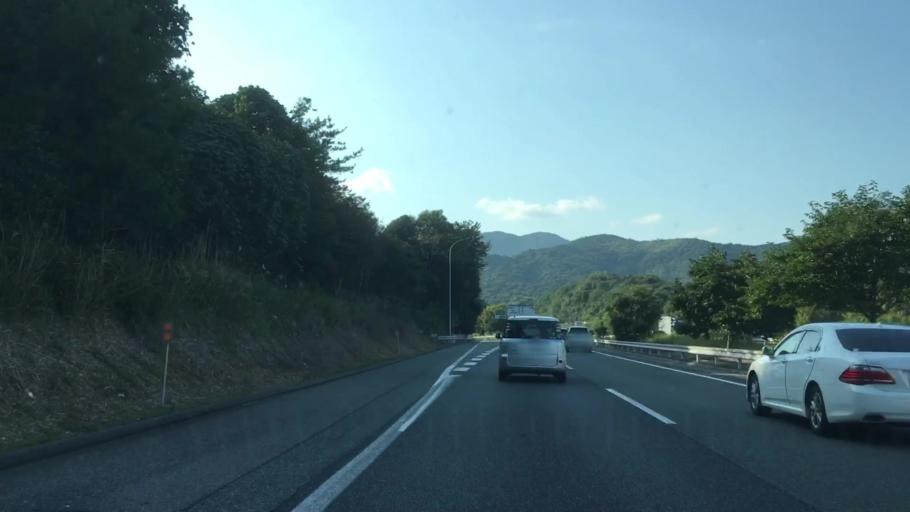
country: JP
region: Yamaguchi
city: Hofu
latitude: 34.0684
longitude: 131.6878
